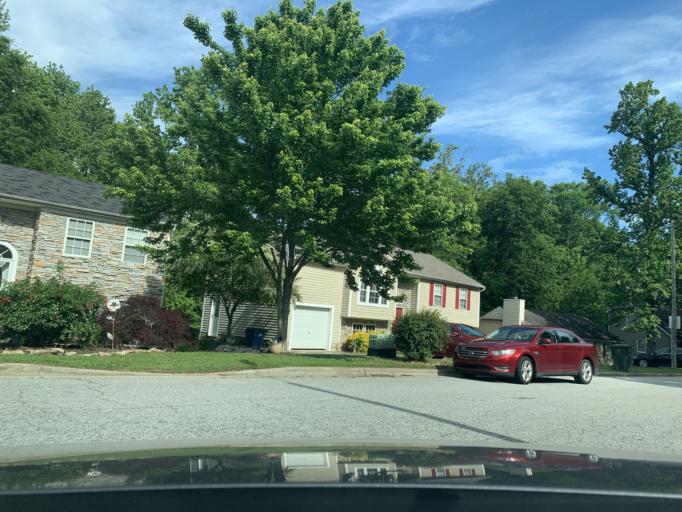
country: US
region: North Carolina
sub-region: Wake County
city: Garner
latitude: 35.7404
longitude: -78.6049
